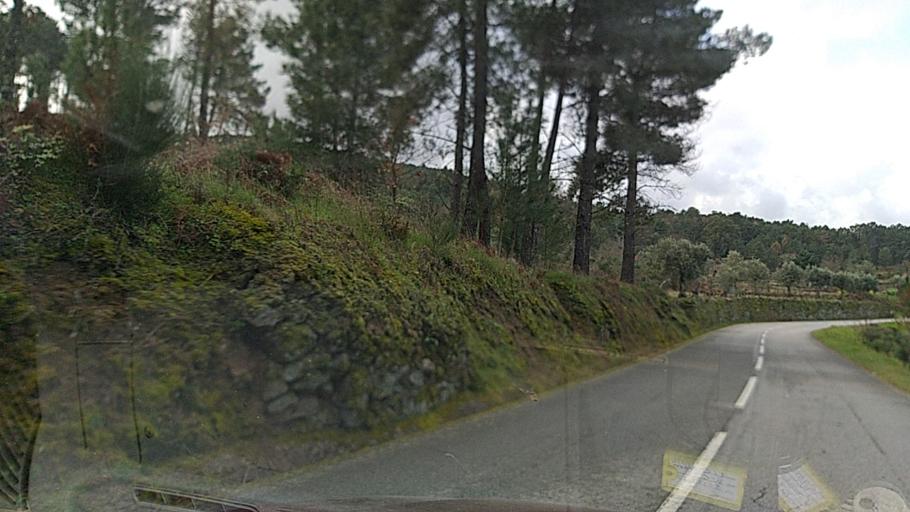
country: PT
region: Guarda
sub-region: Fornos de Algodres
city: Fornos de Algodres
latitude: 40.6671
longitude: -7.6146
